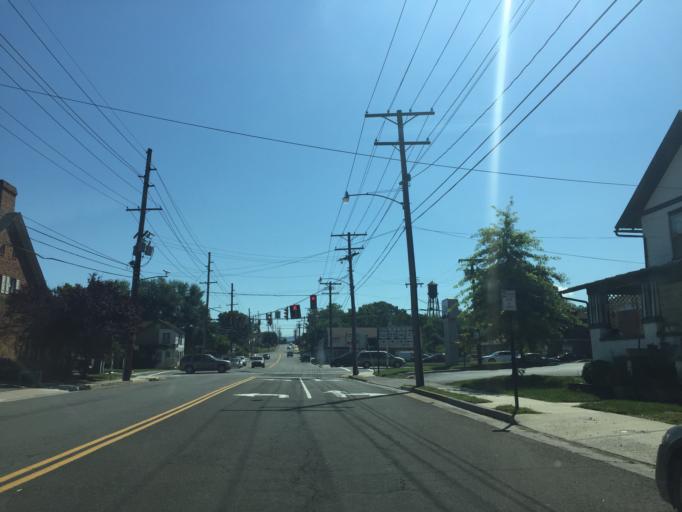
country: US
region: Virginia
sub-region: Warren County
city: Front Royal
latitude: 38.9264
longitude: -78.1922
